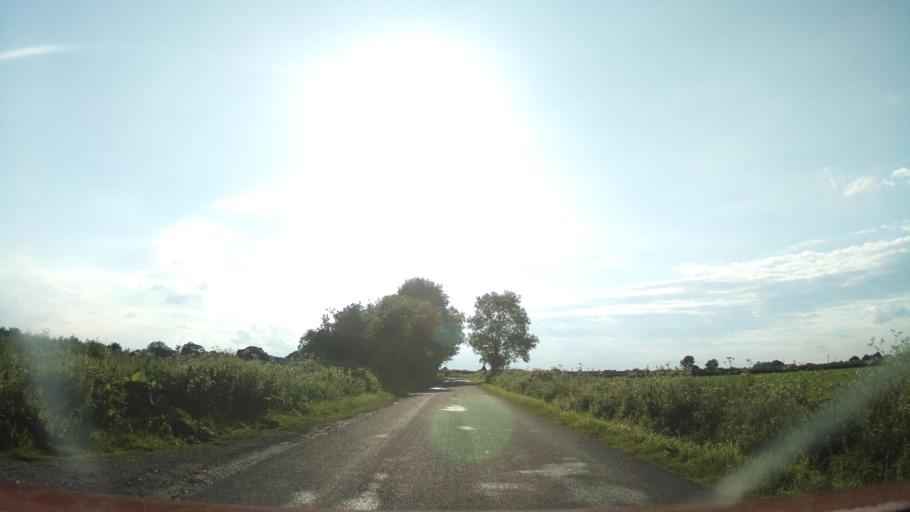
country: GB
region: England
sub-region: Lincolnshire
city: Navenby
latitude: 53.1176
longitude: -0.6336
